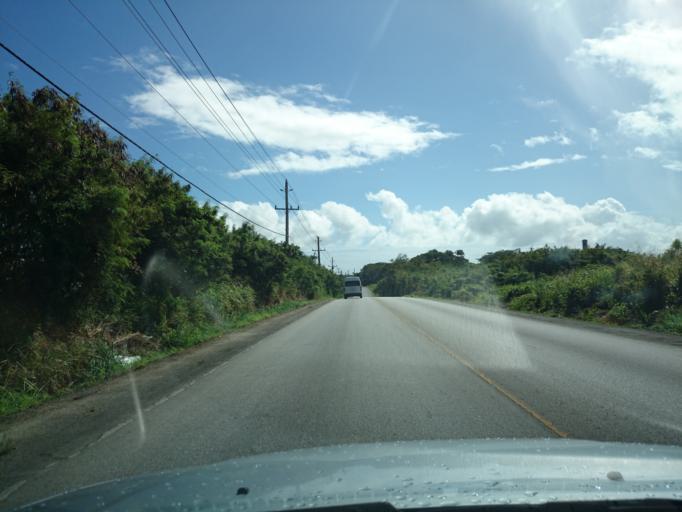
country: BB
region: Saint James
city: Holetown
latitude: 13.2069
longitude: -59.6175
